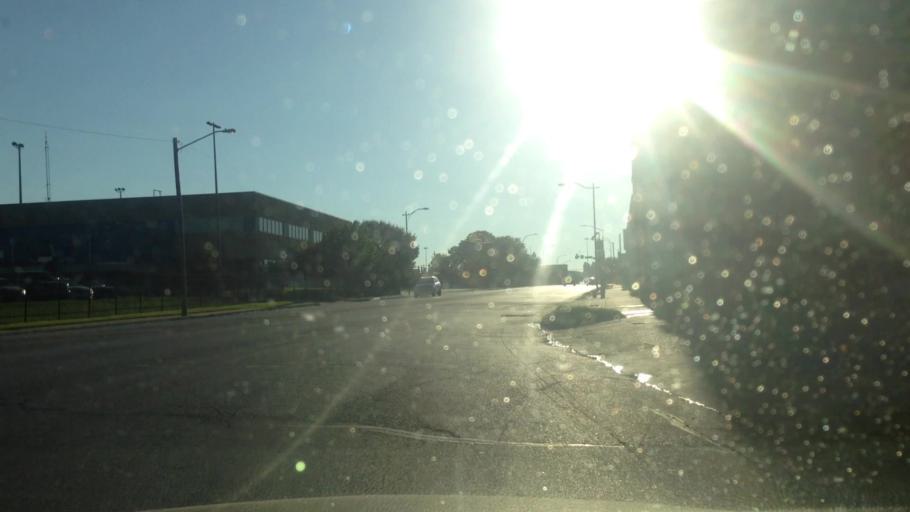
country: US
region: Texas
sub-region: Tarrant County
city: Fort Worth
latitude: 32.7462
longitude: -97.3101
